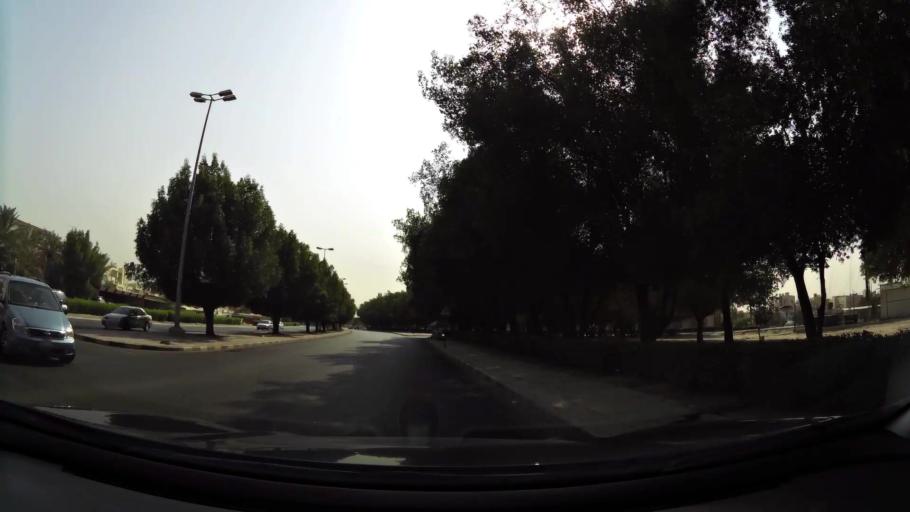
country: KW
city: Bayan
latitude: 29.2966
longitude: 48.0501
